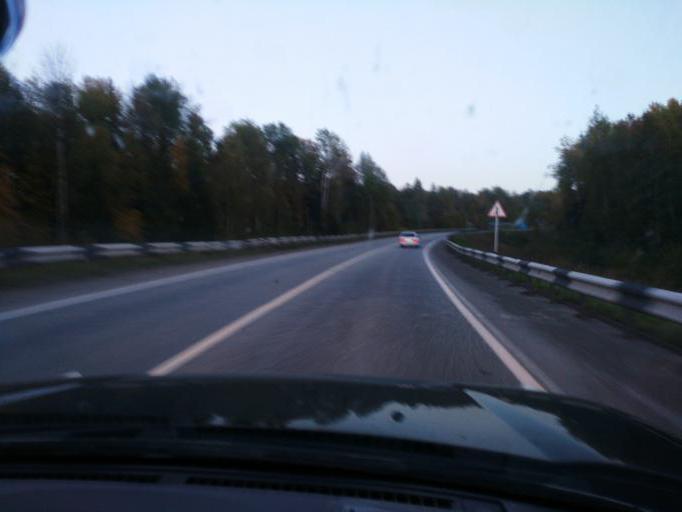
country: RU
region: Perm
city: Verkhnechusovskiye Gorodki
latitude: 58.2924
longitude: 56.8943
